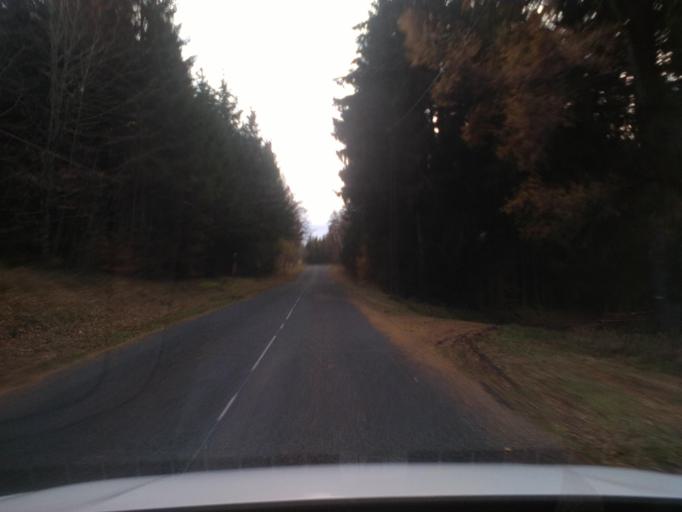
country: FR
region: Lorraine
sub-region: Departement des Vosges
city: Senones
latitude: 48.3776
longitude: 7.0960
